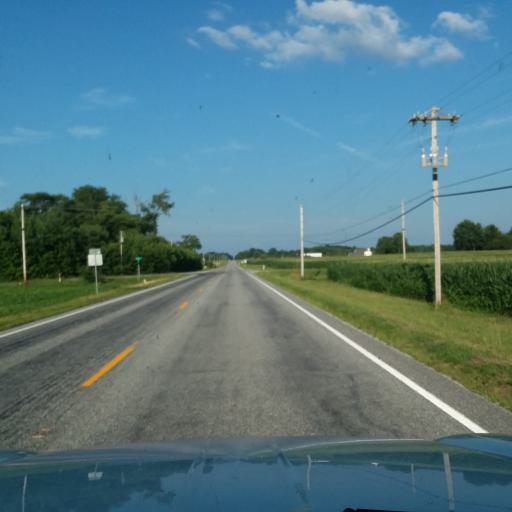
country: US
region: Indiana
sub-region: Johnson County
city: Franklin
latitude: 39.4117
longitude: -86.0322
